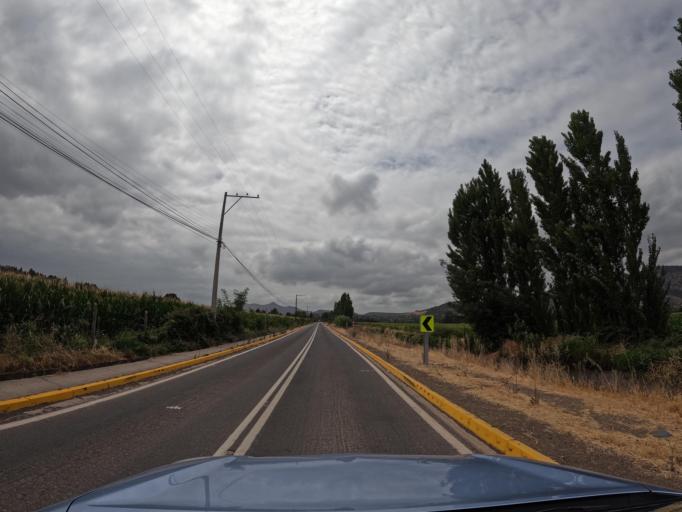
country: CL
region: Maule
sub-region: Provincia de Curico
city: Teno
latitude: -34.7764
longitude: -71.1807
